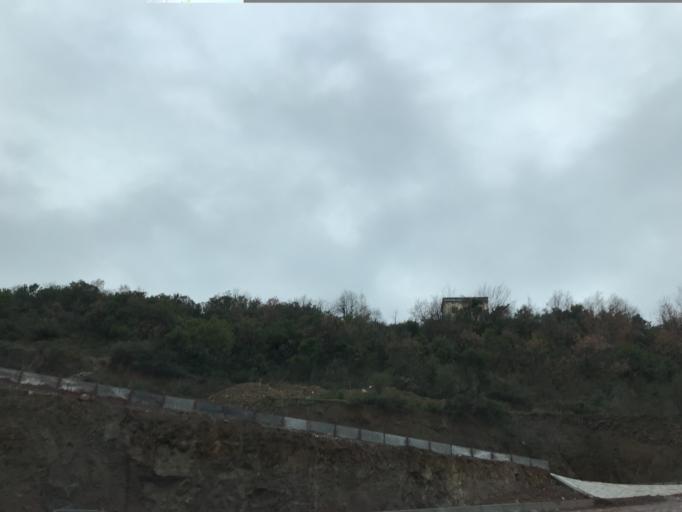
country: TR
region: Yalova
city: Termal
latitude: 40.5969
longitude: 29.1696
